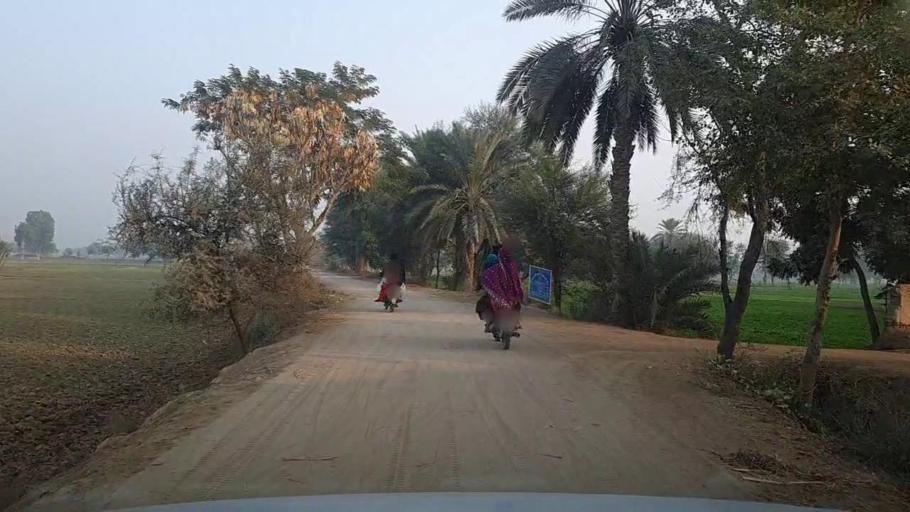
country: PK
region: Sindh
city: Bozdar
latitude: 27.0824
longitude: 68.5678
